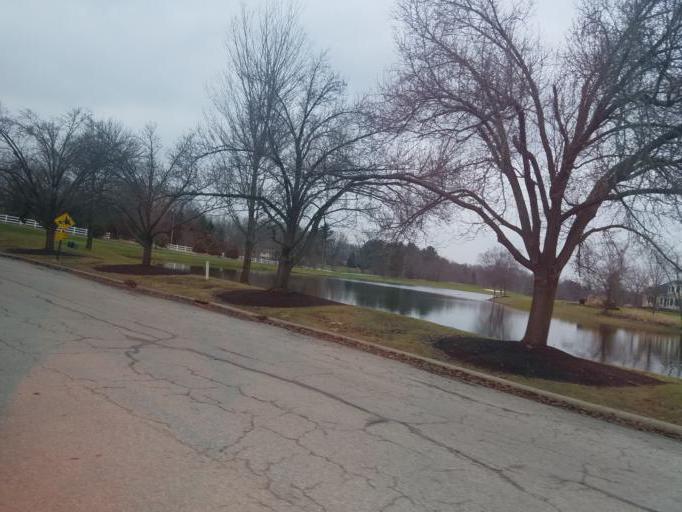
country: US
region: Ohio
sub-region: Franklin County
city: Westerville
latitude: 40.1635
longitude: -82.9508
